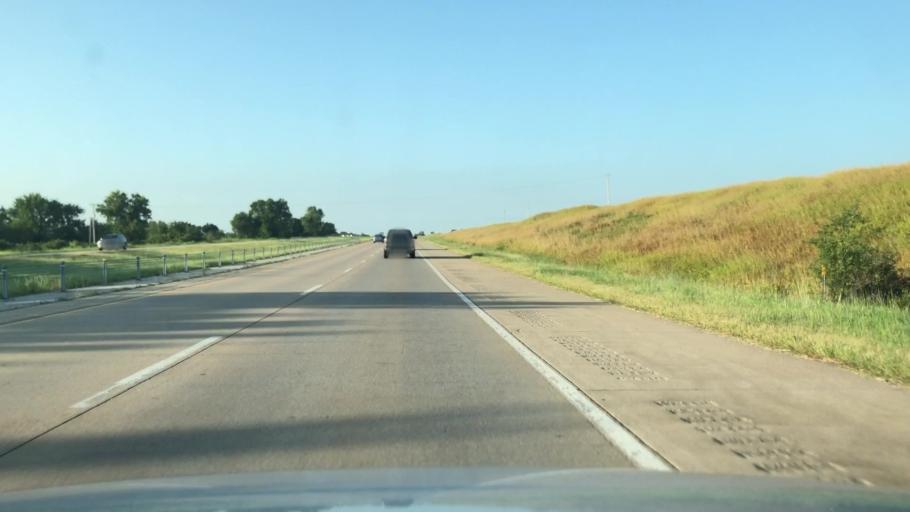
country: US
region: Oklahoma
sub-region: Washington County
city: Bartlesville
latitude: 36.6246
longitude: -95.9357
